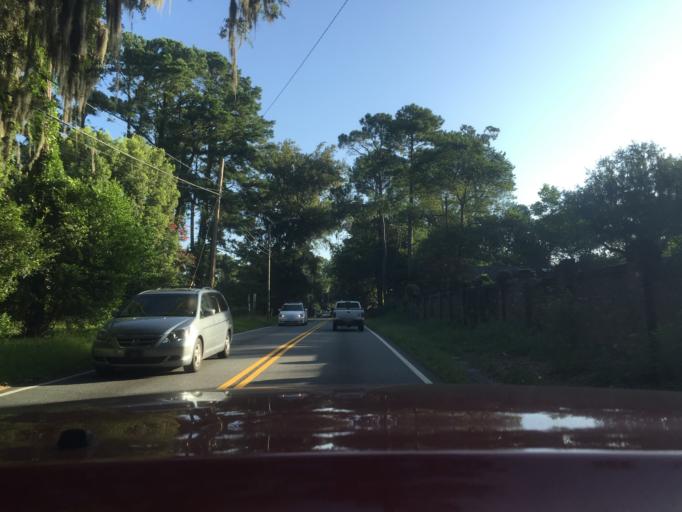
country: US
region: Georgia
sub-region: Chatham County
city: Thunderbolt
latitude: 32.0170
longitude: -81.0974
